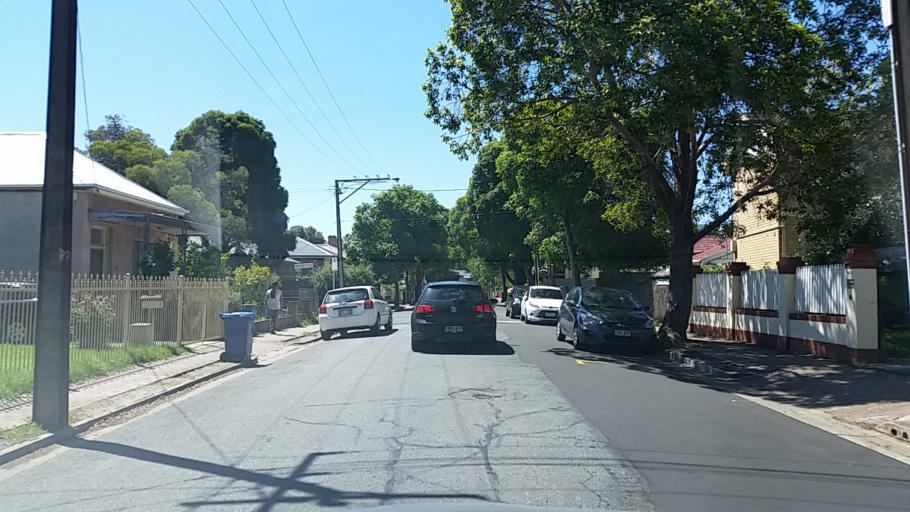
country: AU
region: South Australia
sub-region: Unley
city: Fullarton
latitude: -34.9463
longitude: 138.6212
